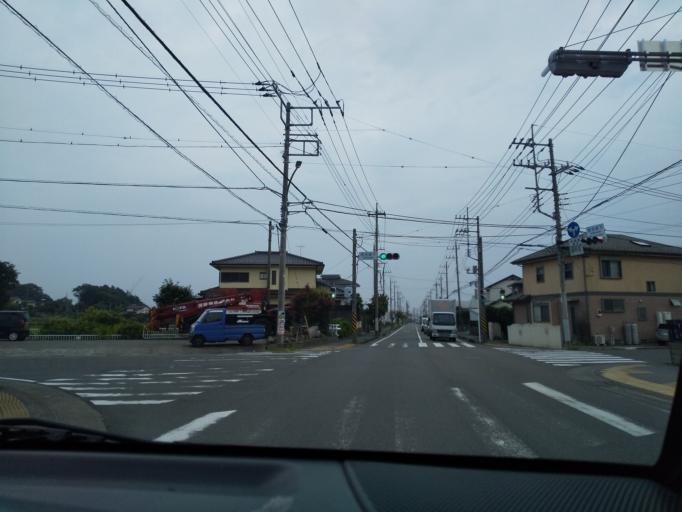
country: JP
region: Kanagawa
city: Atsugi
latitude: 35.4038
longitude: 139.3871
